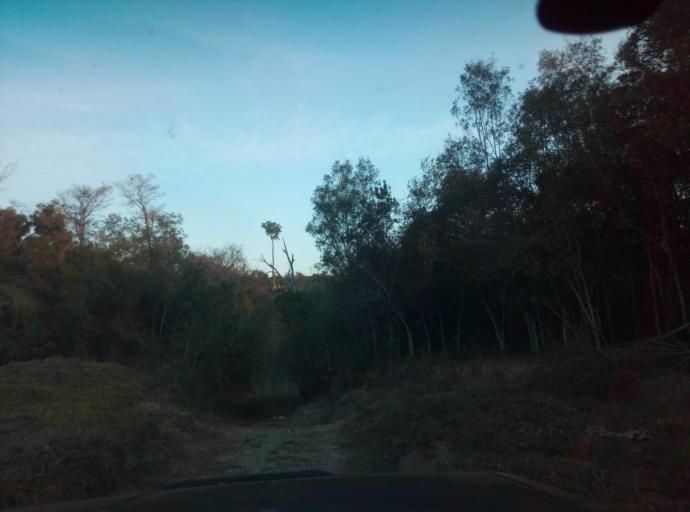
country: PY
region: Caaguazu
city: Yhu
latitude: -25.1984
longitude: -56.1108
